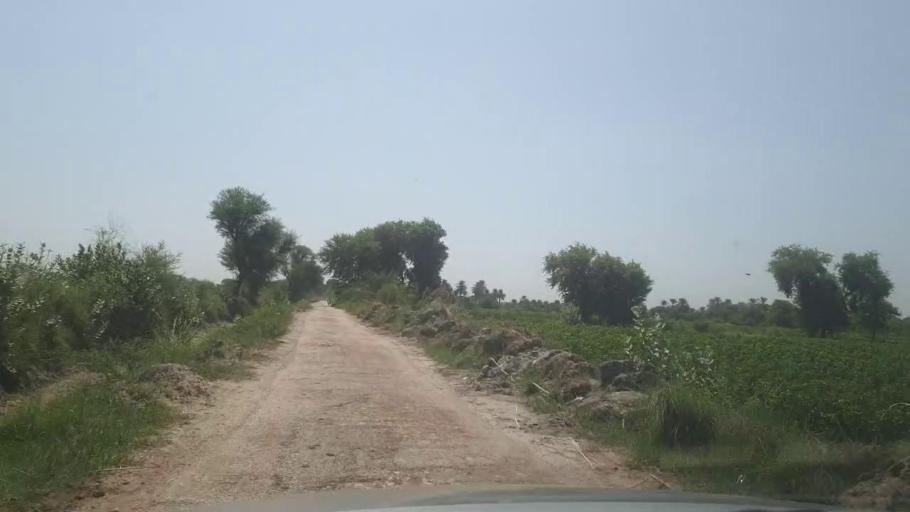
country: PK
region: Sindh
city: Khairpur
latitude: 27.3619
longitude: 69.0300
